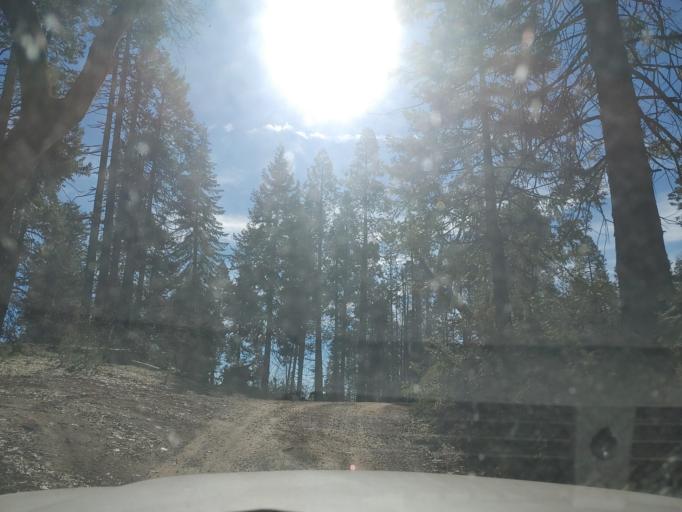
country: US
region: California
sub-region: Madera County
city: Ahwahnee
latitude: 37.4419
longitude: -119.6553
